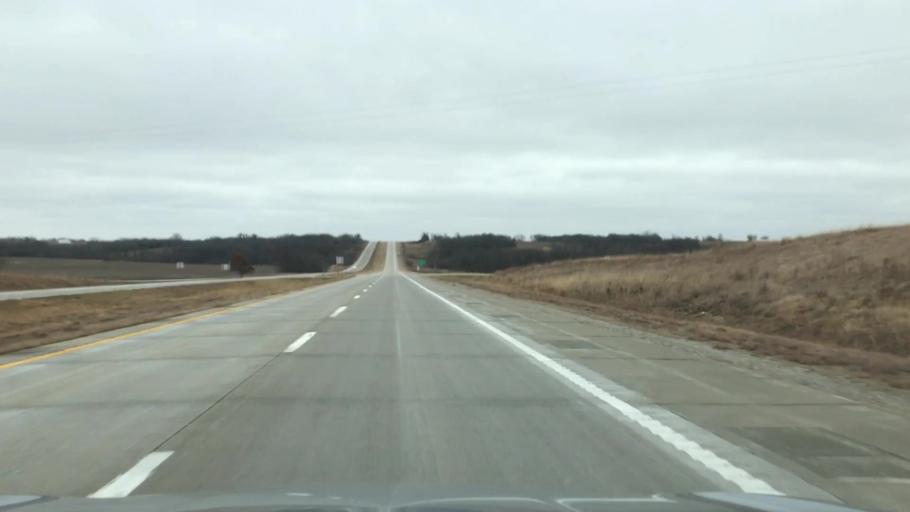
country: US
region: Missouri
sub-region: Livingston County
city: Chillicothe
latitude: 39.7351
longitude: -93.7613
